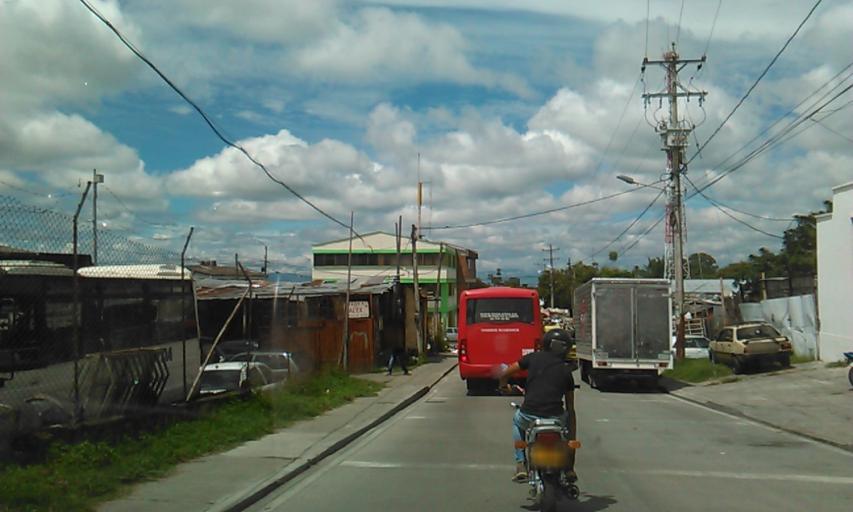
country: CO
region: Quindio
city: Armenia
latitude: 4.5151
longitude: -75.6881
